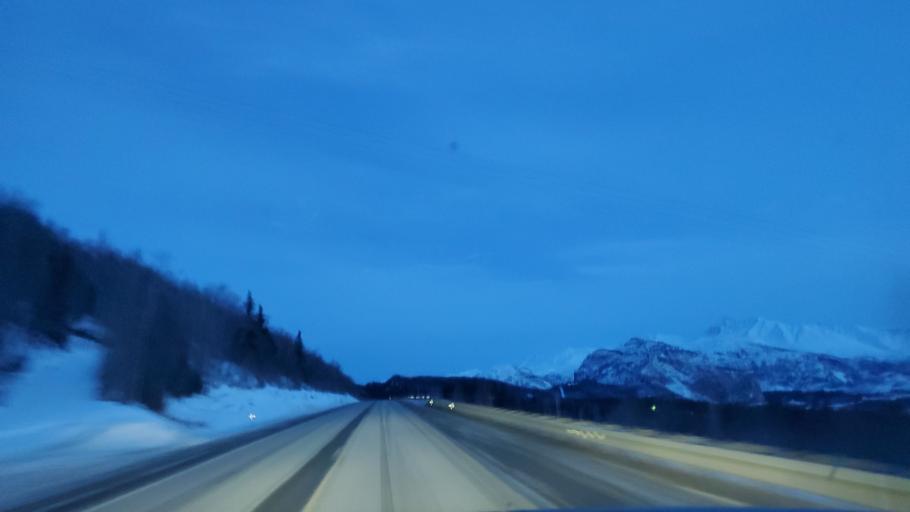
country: US
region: Alaska
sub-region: Matanuska-Susitna Borough
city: Sutton-Alpine
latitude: 61.7973
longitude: -147.7469
